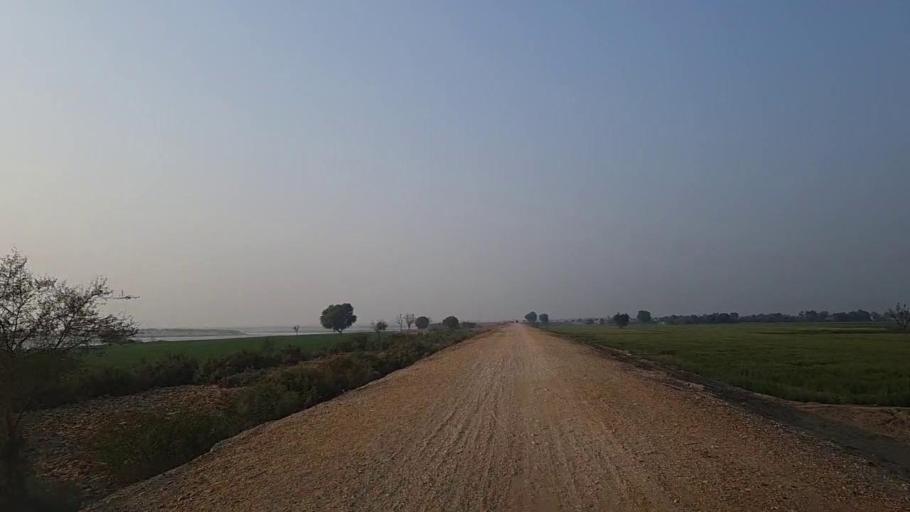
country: PK
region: Sindh
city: Sann
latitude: 26.1283
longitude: 68.1405
